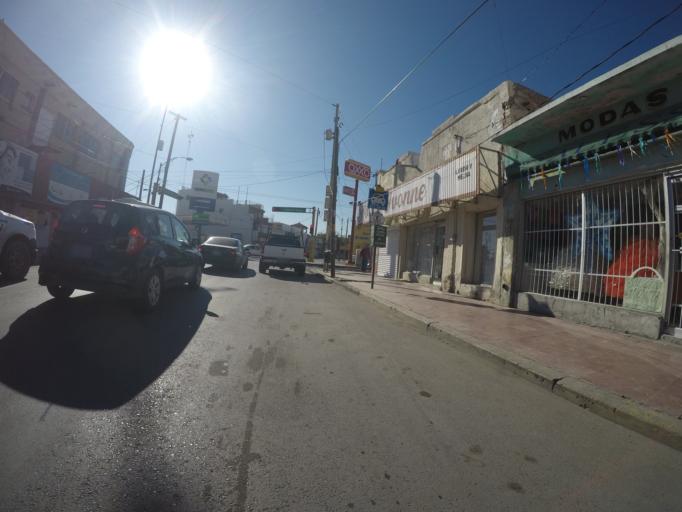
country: MX
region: Chihuahua
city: Ciudad Juarez
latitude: 31.7433
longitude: -106.4815
